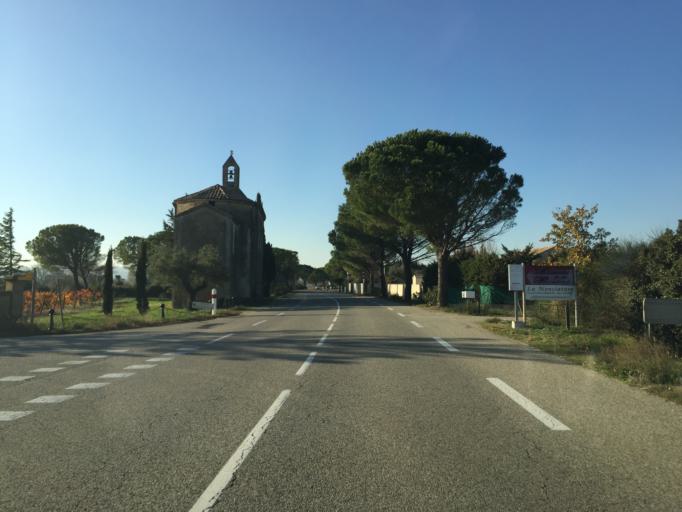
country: FR
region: Provence-Alpes-Cote d'Azur
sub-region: Departement du Vaucluse
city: Sainte-Cecile-les-Vignes
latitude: 44.2424
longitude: 4.8981
